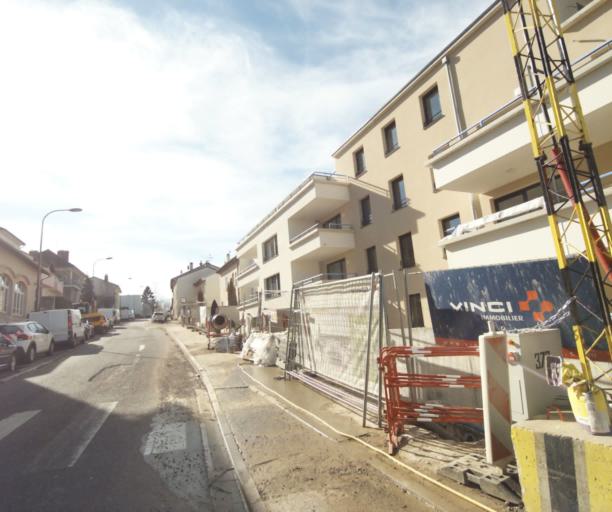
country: FR
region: Lorraine
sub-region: Departement de Meurthe-et-Moselle
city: Villers-les-Nancy
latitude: 48.6710
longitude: 6.1424
